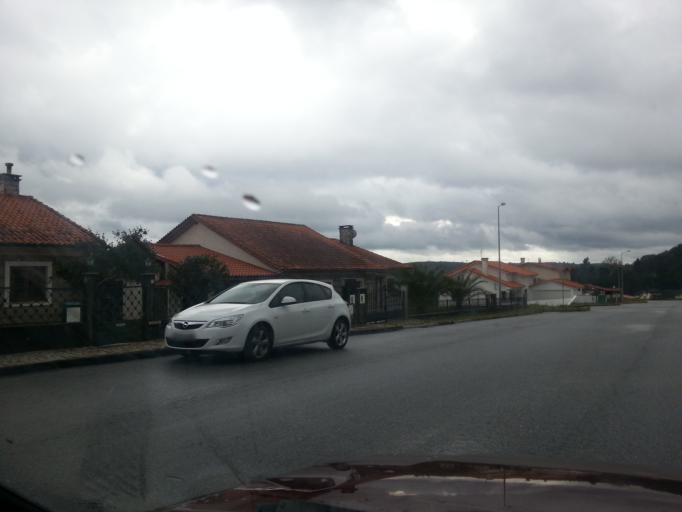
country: PT
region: Guarda
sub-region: Fornos de Algodres
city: Fornos de Algodres
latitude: 40.6163
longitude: -7.5208
